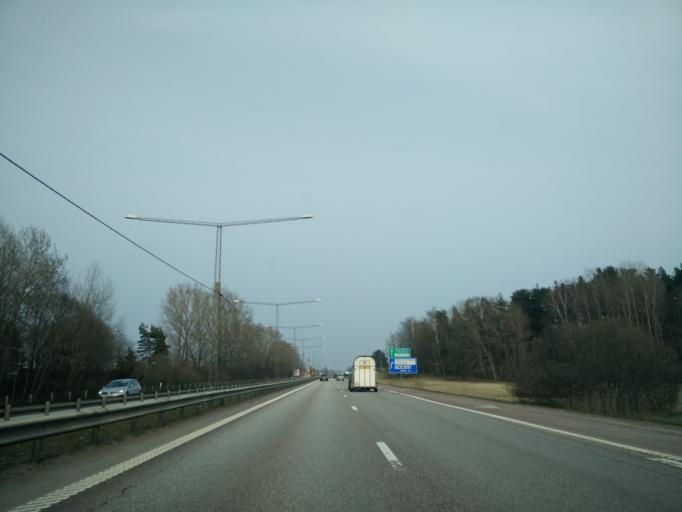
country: SE
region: Vaermland
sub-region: Karlstads Kommun
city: Karlstad
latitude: 59.3800
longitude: 13.4519
